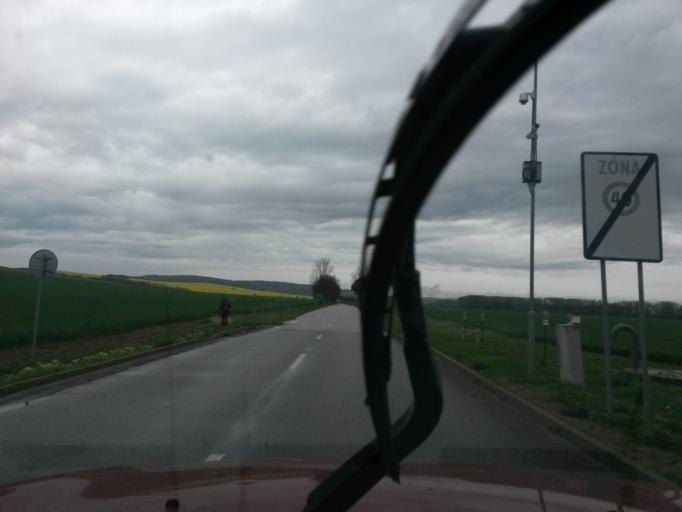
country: HU
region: Borsod-Abauj-Zemplen
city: Gonc
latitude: 48.5463
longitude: 21.2232
